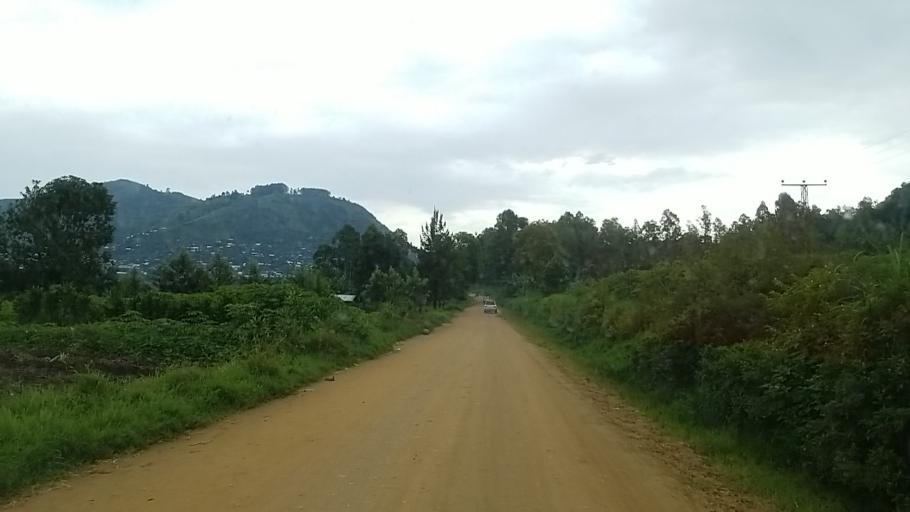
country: CD
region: Nord Kivu
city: Sake
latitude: -1.7007
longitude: 29.0145
